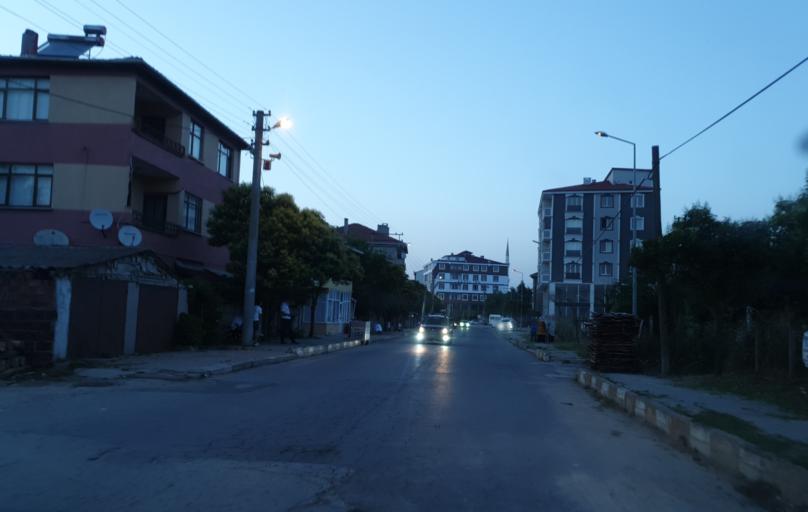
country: TR
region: Tekirdag
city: Saray
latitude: 41.3713
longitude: 27.9303
